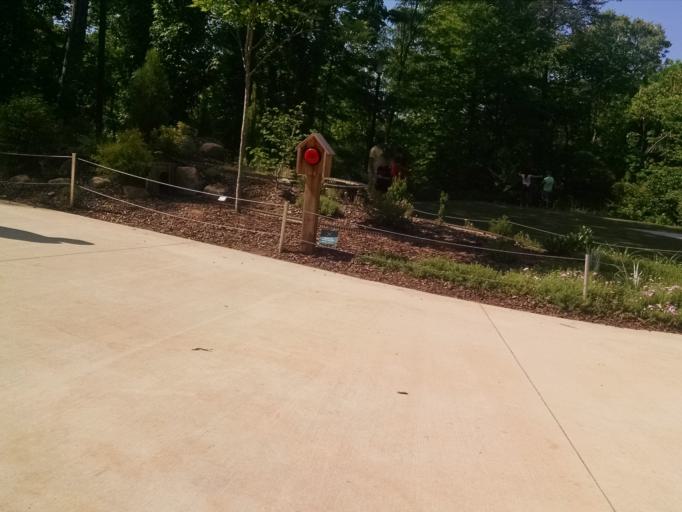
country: US
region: Georgia
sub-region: Hall County
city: Gainesville
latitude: 34.3342
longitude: -83.8186
